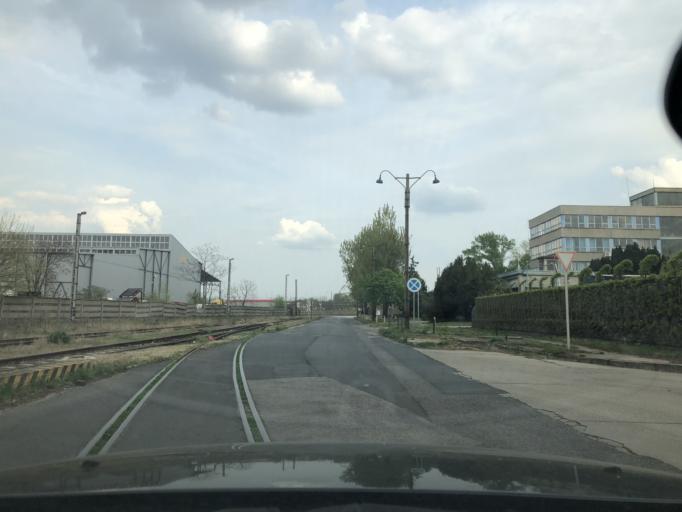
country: HU
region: Budapest
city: Budapest XXI. keruelet
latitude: 47.4416
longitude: 19.0651
